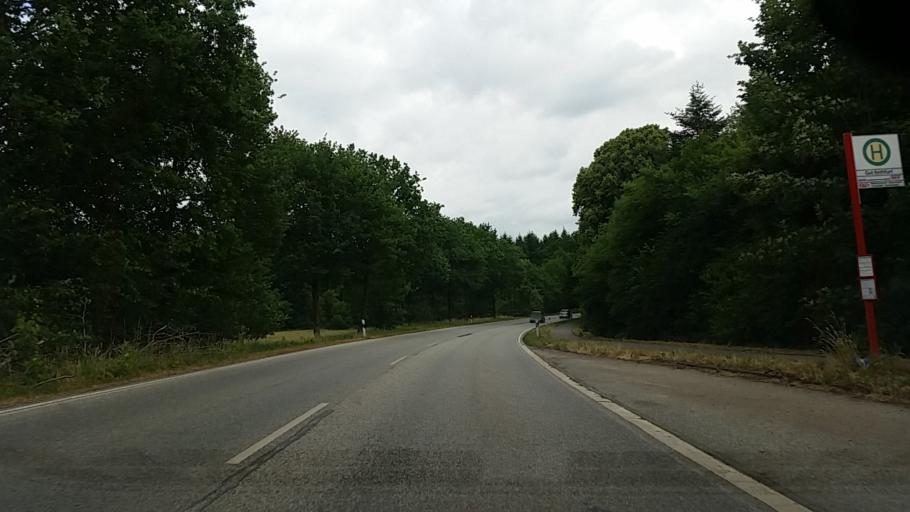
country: DE
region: Schleswig-Holstein
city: Kayhude
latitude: 53.7452
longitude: 10.1218
